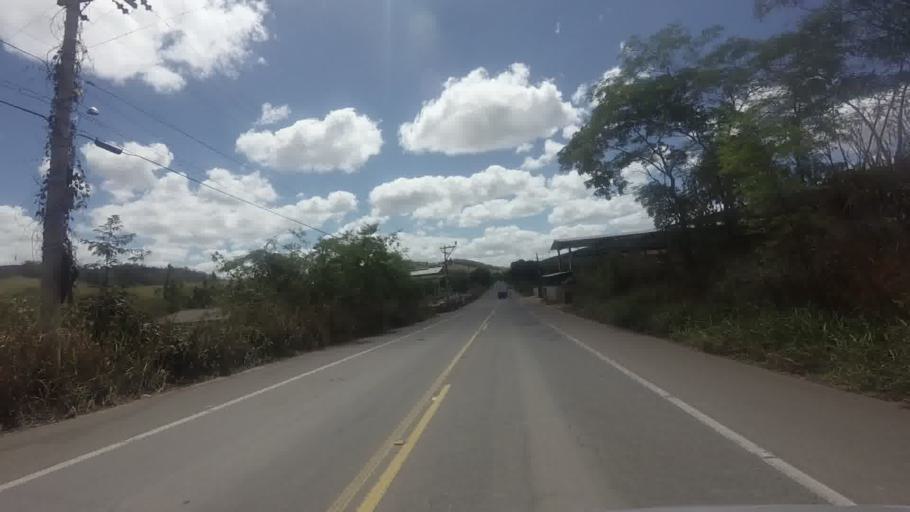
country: BR
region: Rio de Janeiro
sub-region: Santo Antonio De Padua
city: Santo Antonio de Padua
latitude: -21.6446
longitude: -42.2827
